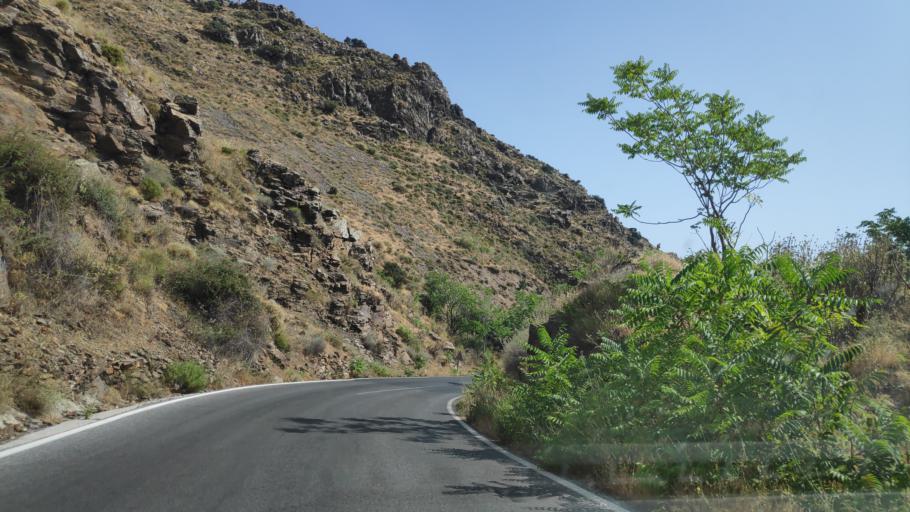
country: ES
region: Andalusia
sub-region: Provincia de Granada
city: Pampaneira
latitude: 36.9311
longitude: -3.3641
